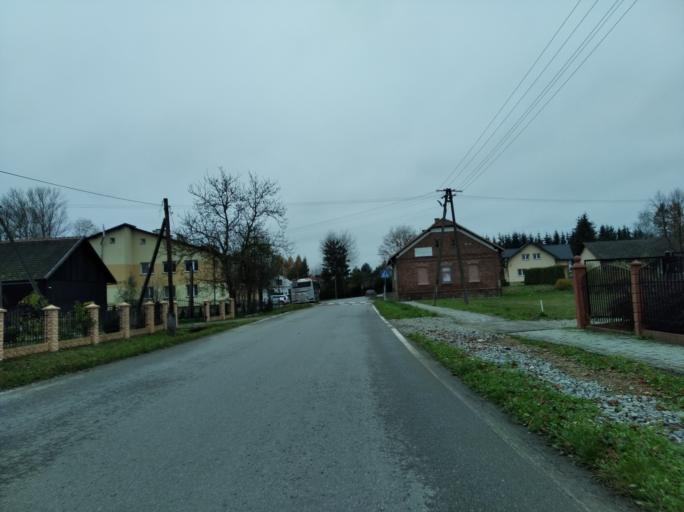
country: PL
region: Subcarpathian Voivodeship
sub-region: Powiat krosnienski
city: Leki
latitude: 49.8054
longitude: 21.6639
